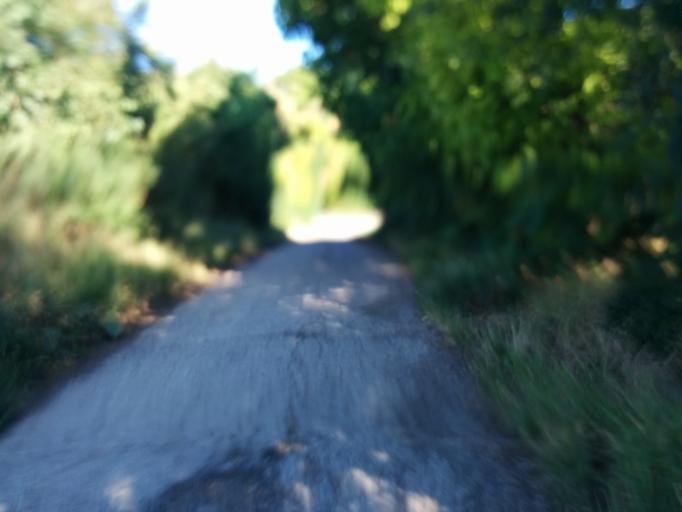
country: AT
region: Lower Austria
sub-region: Politischer Bezirk Modling
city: Neu-Guntramsdorf
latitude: 48.0689
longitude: 16.3020
